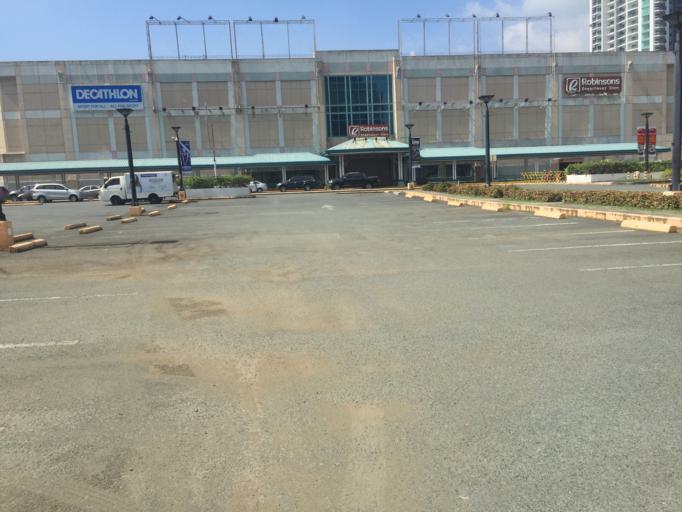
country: PH
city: Sambayanihan People's Village
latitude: 14.4171
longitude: 121.0391
